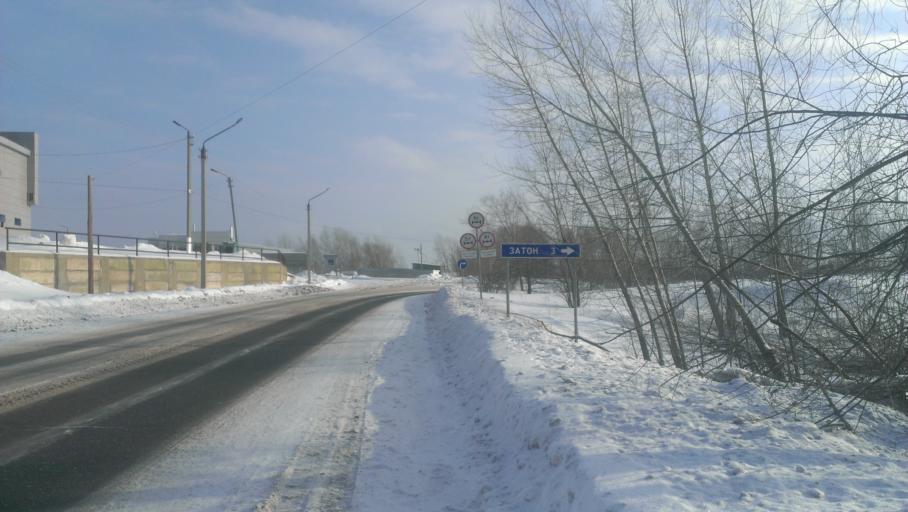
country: RU
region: Altai Krai
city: Zaton
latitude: 53.3148
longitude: 83.8305
